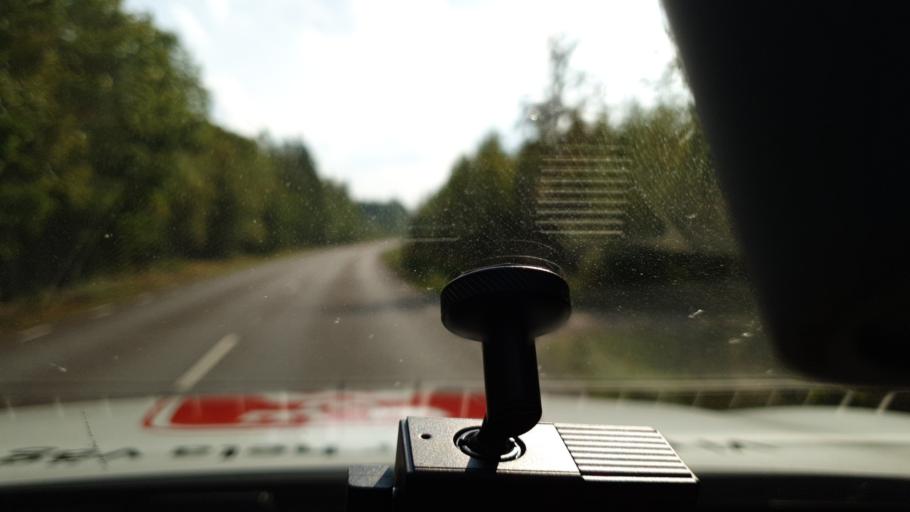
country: SE
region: Kalmar
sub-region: Vimmerby Kommun
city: Vimmerby
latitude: 57.6987
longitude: 15.8422
